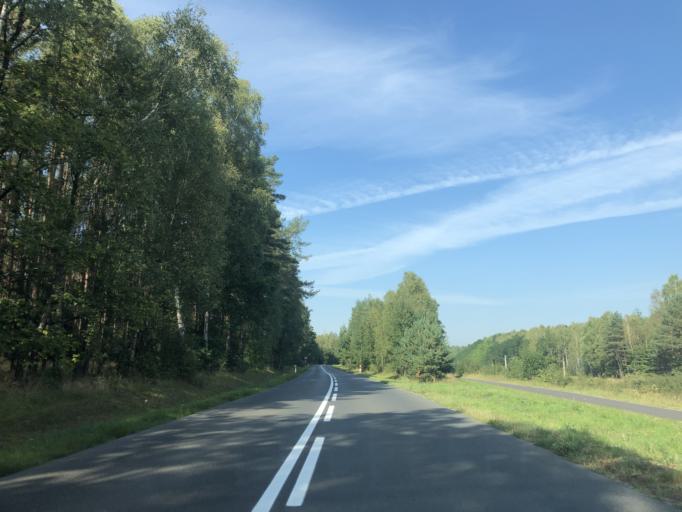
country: PL
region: Greater Poland Voivodeship
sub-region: Powiat pilski
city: Kaczory
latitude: 53.1270
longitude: 16.8109
